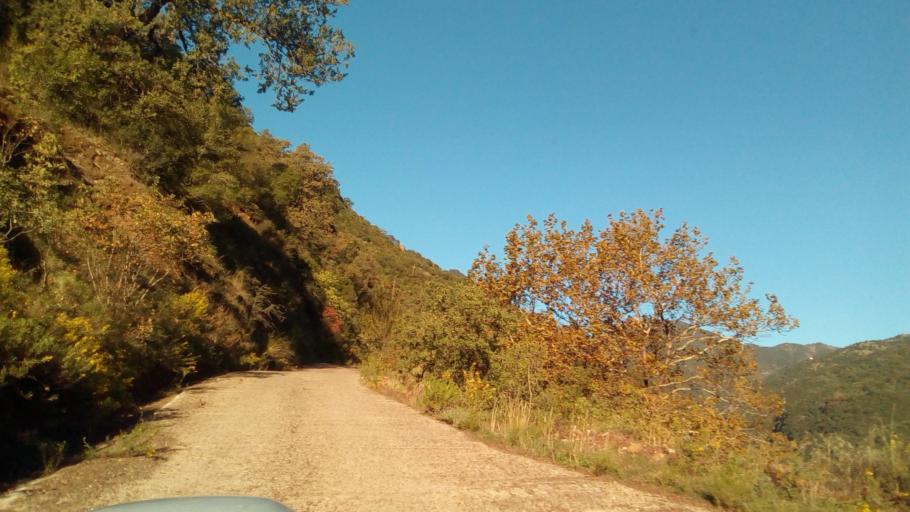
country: GR
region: West Greece
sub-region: Nomos Aitolias kai Akarnanias
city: Nafpaktos
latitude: 38.4670
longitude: 21.8717
